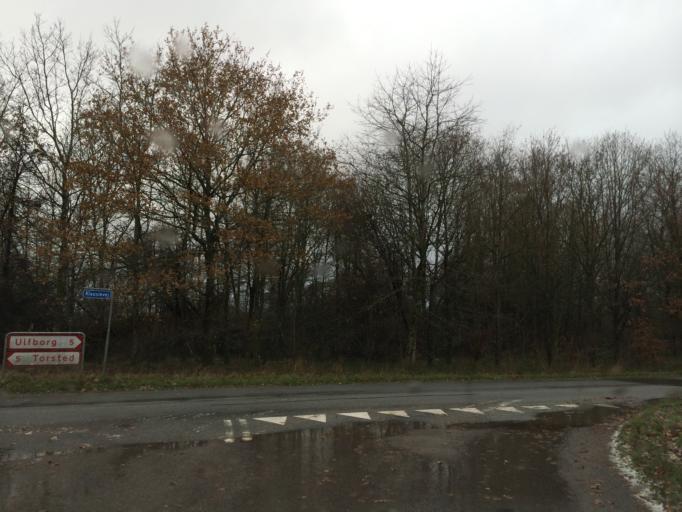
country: DK
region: Central Jutland
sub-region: Holstebro Kommune
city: Ulfborg
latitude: 56.2446
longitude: 8.3833
